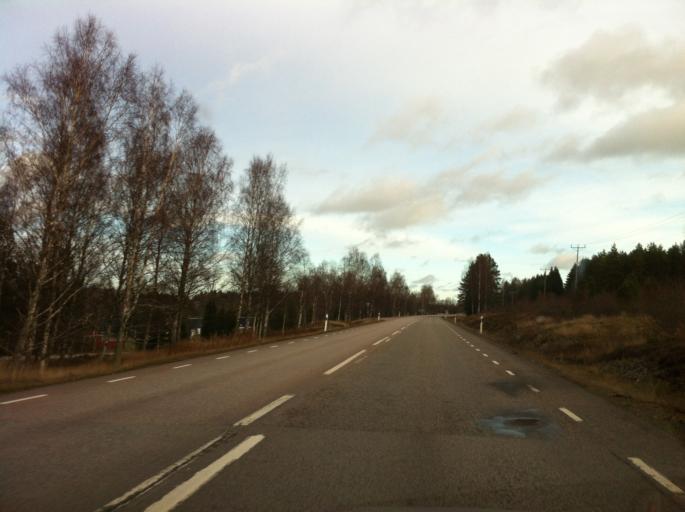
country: SE
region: Kronoberg
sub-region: Uppvidinge Kommun
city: Aseda
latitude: 57.1362
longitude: 15.2804
